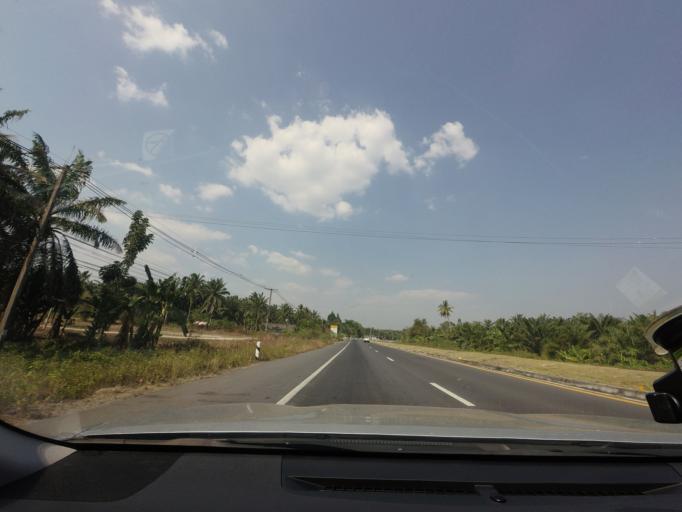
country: TH
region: Phangnga
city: Thap Put
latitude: 8.5361
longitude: 98.7134
